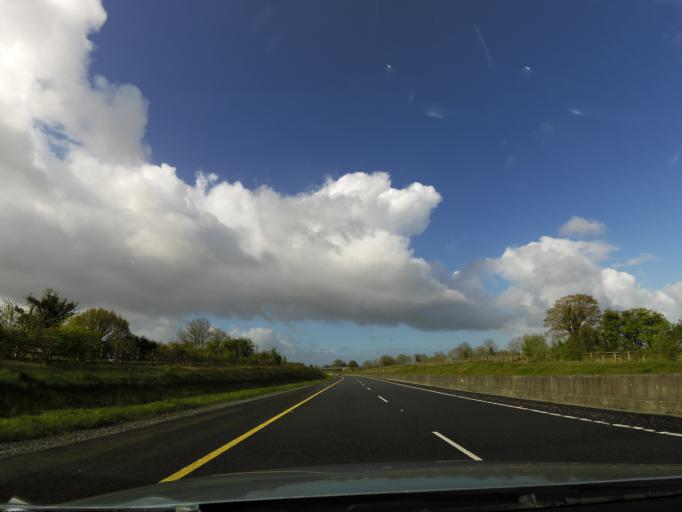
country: IE
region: Munster
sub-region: County Limerick
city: Castleconnell
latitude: 52.6979
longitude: -8.4911
